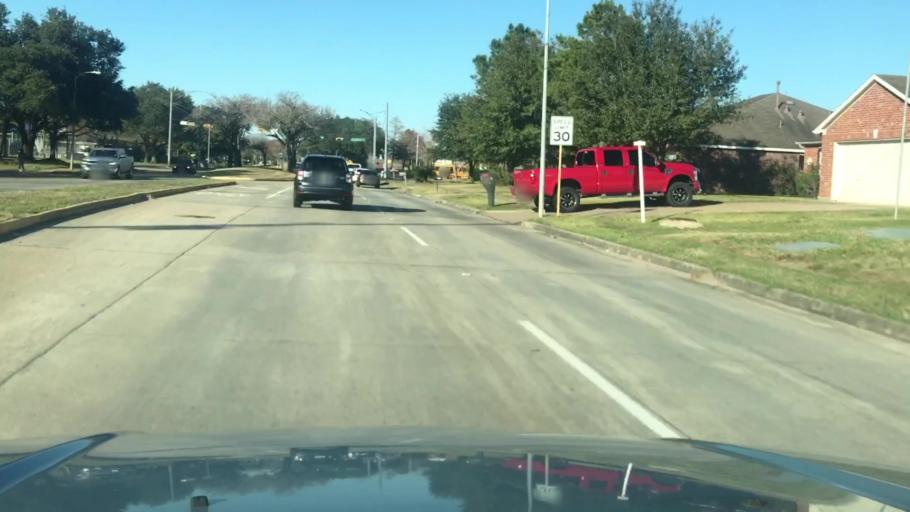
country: US
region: Texas
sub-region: Fort Bend County
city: Cinco Ranch
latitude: 29.8174
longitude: -95.7522
